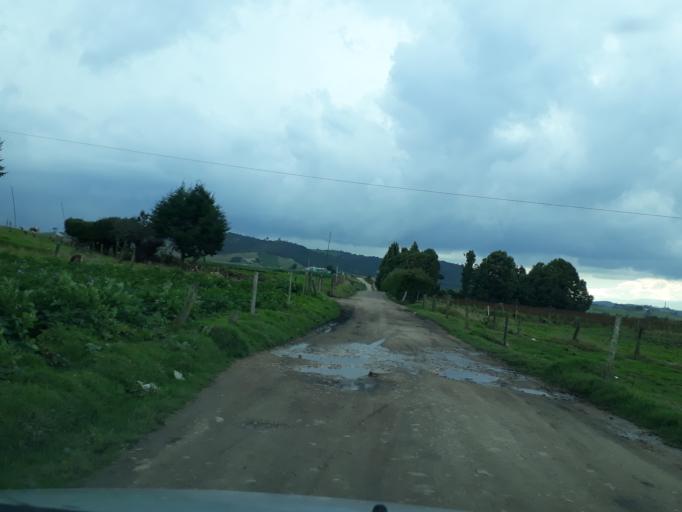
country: CO
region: Cundinamarca
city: Villapinzon
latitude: 5.2404
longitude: -73.6631
